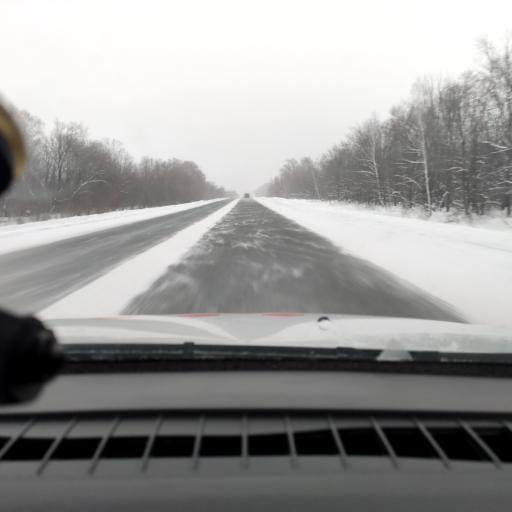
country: RU
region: Samara
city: Kinel'
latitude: 53.2548
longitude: 50.7869
